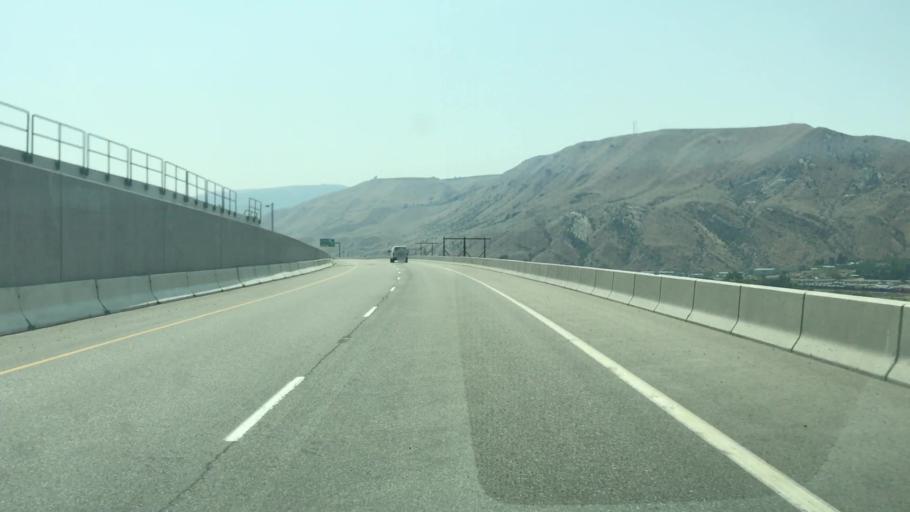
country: US
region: Washington
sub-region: Douglas County
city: East Wenatchee
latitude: 47.4046
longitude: -120.2917
